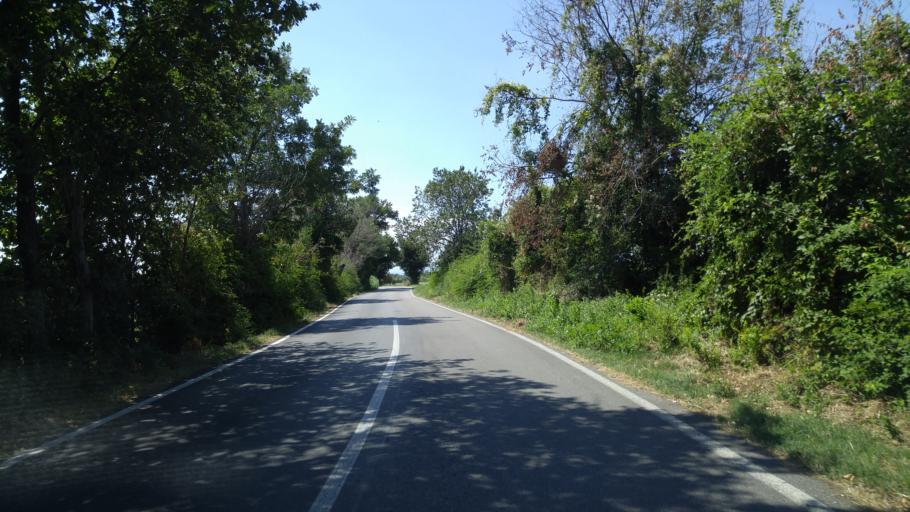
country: IT
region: The Marches
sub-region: Provincia di Pesaro e Urbino
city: Rosciano
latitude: 43.8040
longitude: 12.9874
